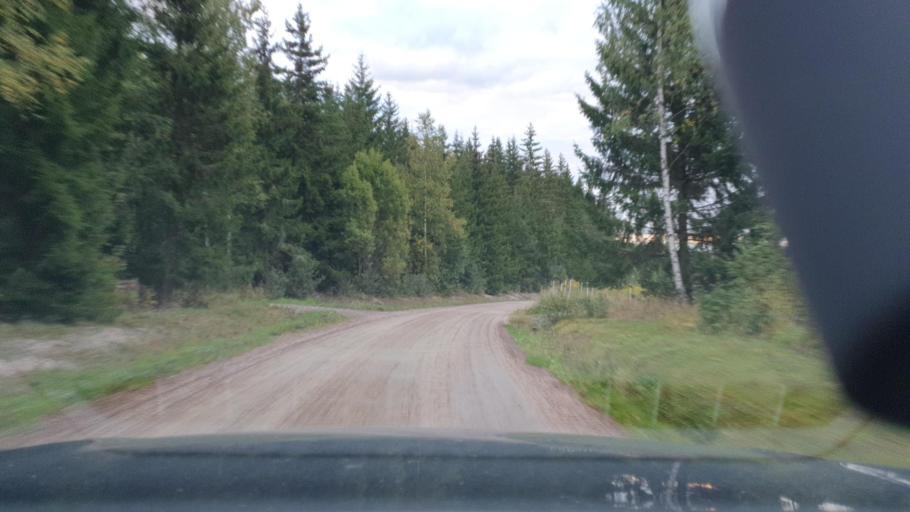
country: SE
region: Vaermland
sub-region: Munkfors Kommun
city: Munkfors
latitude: 59.8310
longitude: 13.4940
